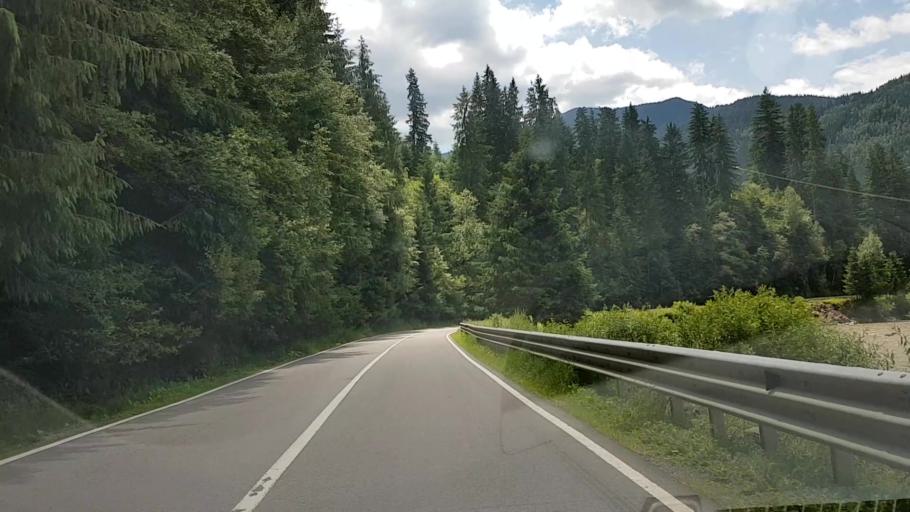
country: RO
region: Suceava
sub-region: Comuna Crucea
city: Crucea
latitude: 47.3533
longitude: 25.6156
